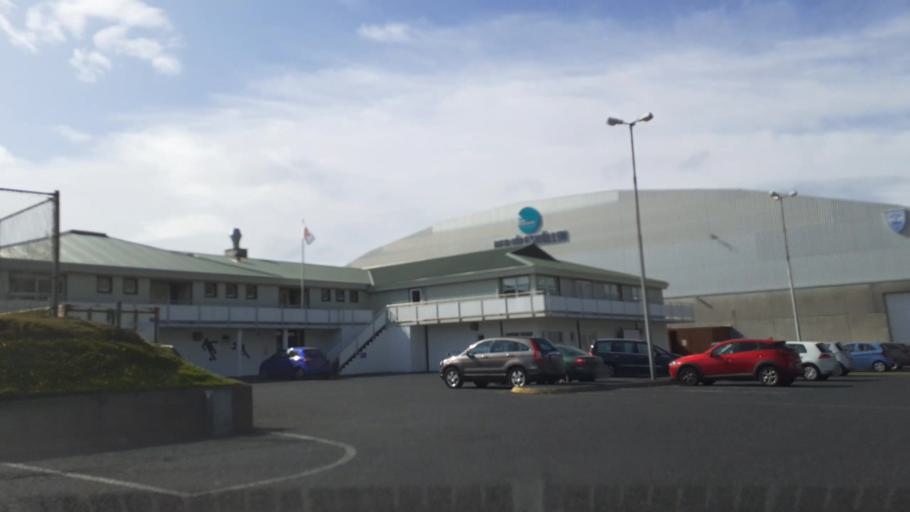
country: IS
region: South
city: Vestmannaeyjar
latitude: 63.4389
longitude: -20.2867
